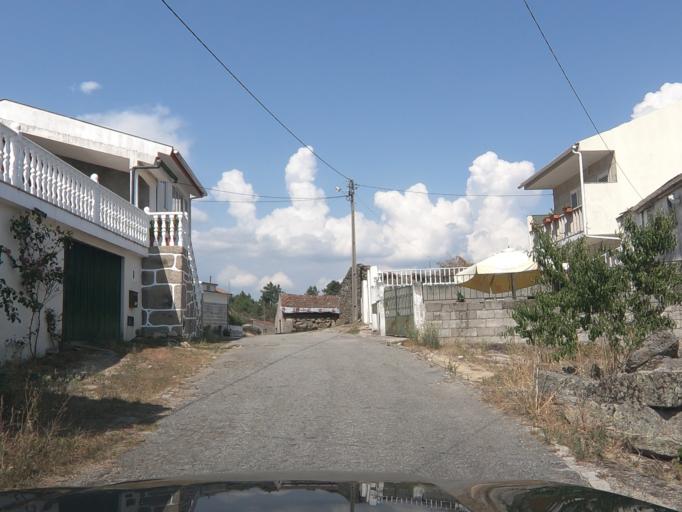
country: PT
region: Vila Real
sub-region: Sabrosa
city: Sabrosa
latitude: 41.3032
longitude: -7.5944
